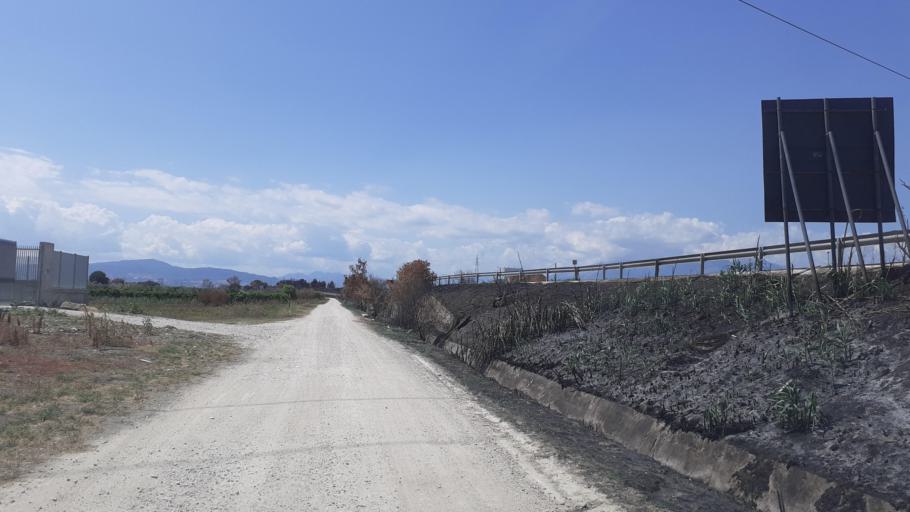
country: IT
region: Abruzzo
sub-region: Provincia di Chieti
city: Fossacesia
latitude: 42.2198
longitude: 14.5006
